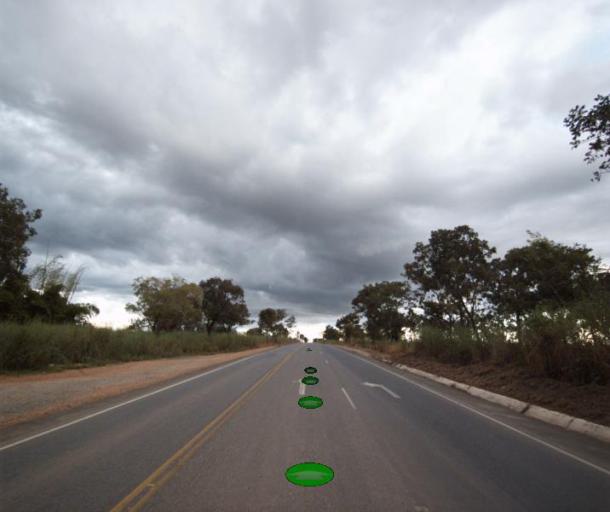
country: BR
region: Goias
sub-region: Uruacu
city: Uruacu
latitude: -14.7143
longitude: -49.2276
